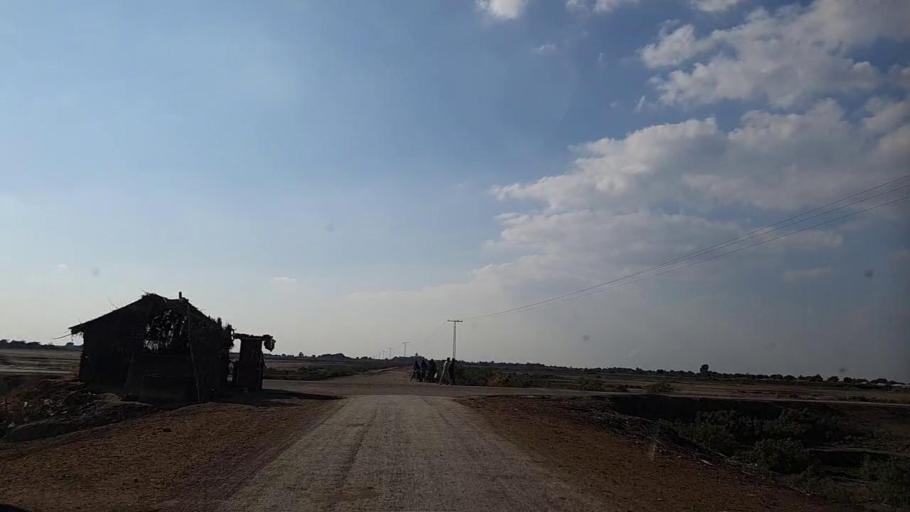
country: PK
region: Sindh
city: Pithoro
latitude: 25.6524
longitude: 69.2459
